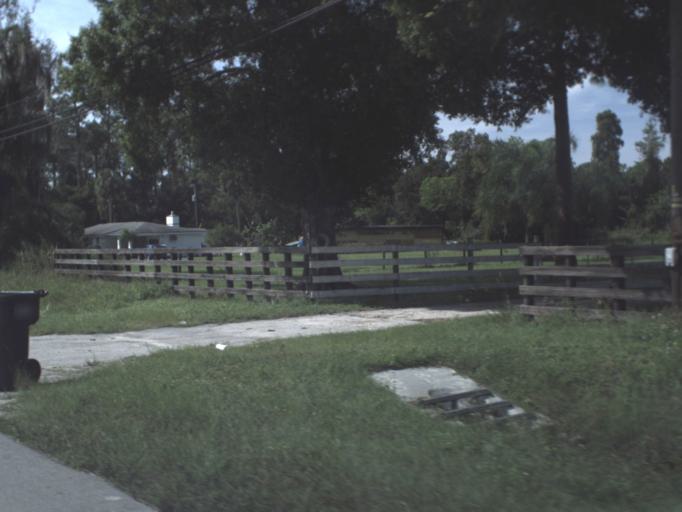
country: US
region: Florida
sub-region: Lee County
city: Fort Myers Shores
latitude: 26.7461
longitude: -81.7610
